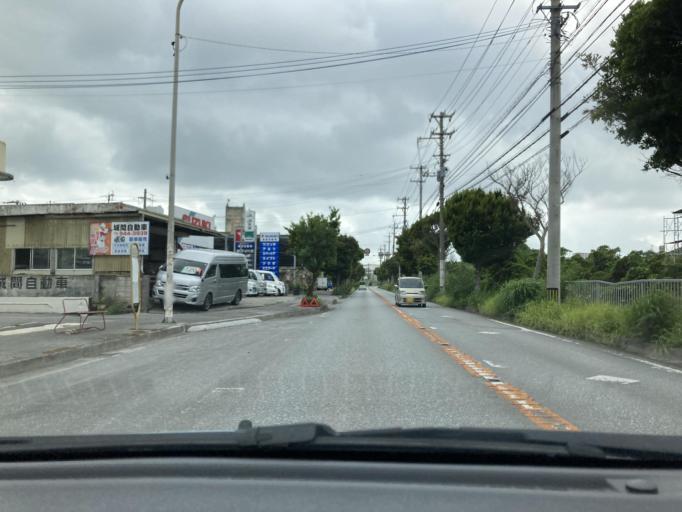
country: JP
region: Okinawa
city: Ginowan
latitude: 26.2333
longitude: 127.7415
